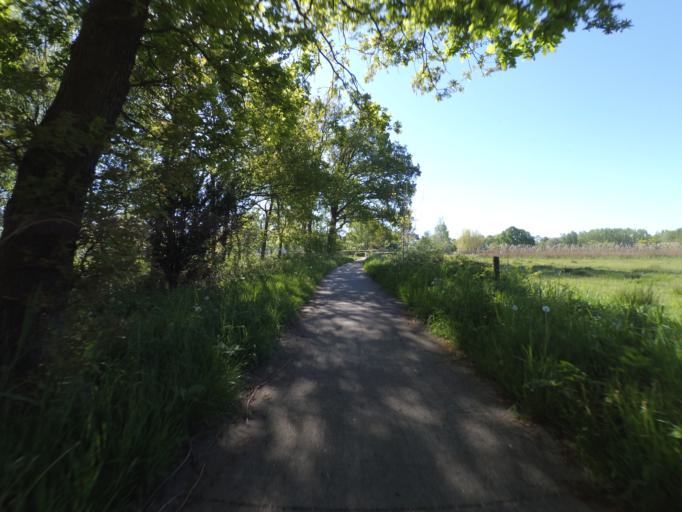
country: NL
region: Gelderland
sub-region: Gemeente Brummen
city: Brummen
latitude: 52.0995
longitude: 6.1180
